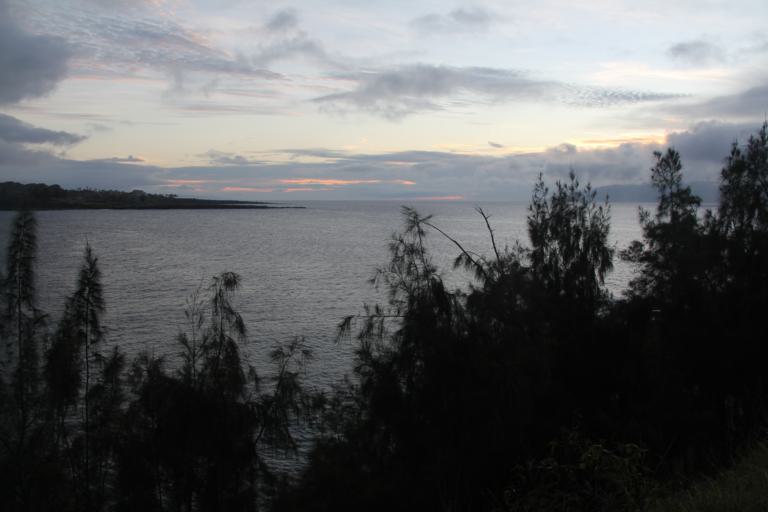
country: US
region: Hawaii
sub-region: Maui County
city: Napili-Honokowai
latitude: 21.0104
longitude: -156.6458
